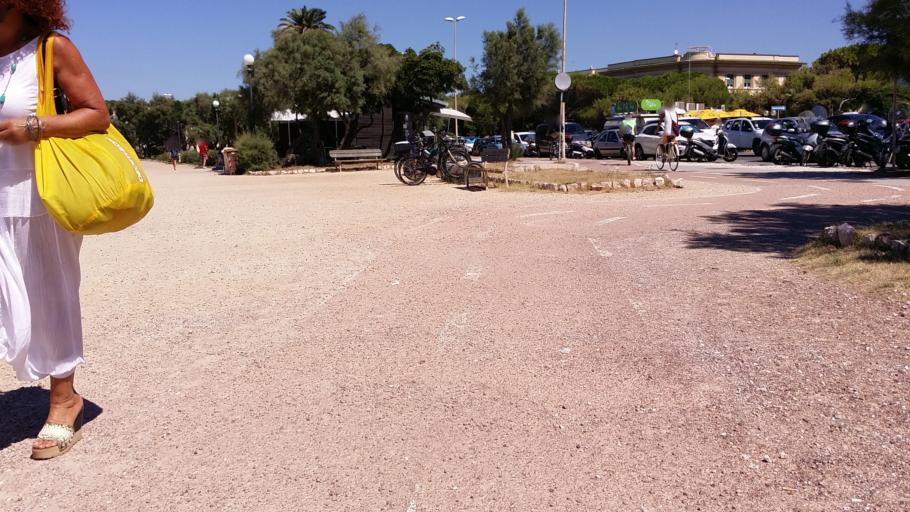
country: IT
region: Tuscany
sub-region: Provincia di Livorno
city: Livorno
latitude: 43.5175
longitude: 10.3163
